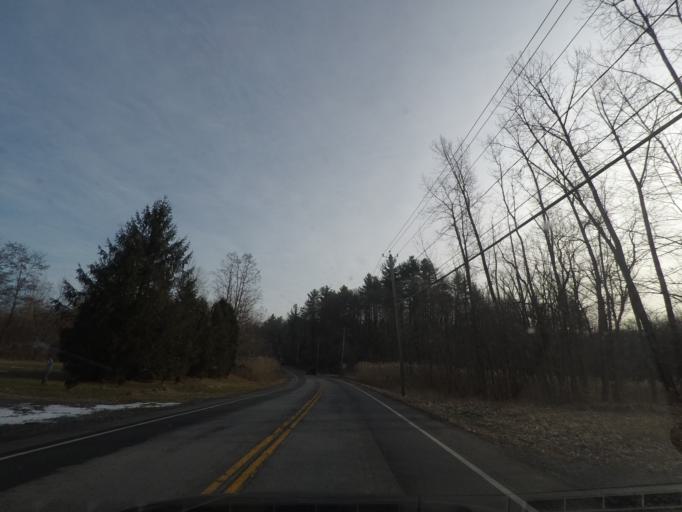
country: US
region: New York
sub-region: Saratoga County
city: Country Knolls
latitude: 42.9852
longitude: -73.7539
